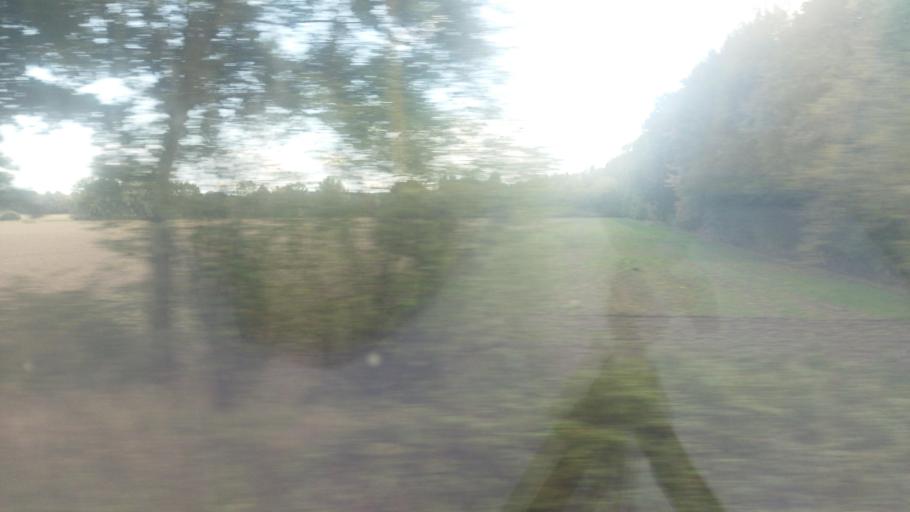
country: DE
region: North Rhine-Westphalia
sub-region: Regierungsbezirk Munster
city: Senden
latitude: 51.9124
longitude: 7.5161
